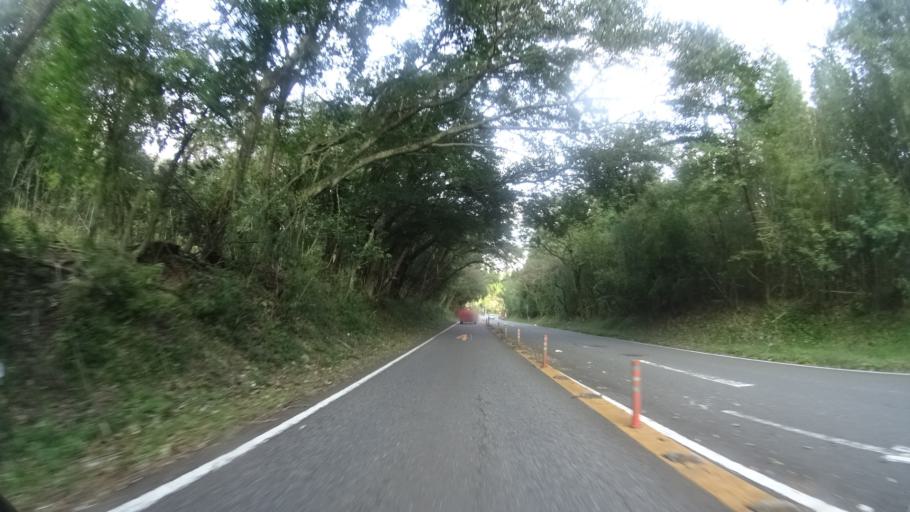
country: JP
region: Oita
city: Beppu
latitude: 33.2738
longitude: 131.4436
